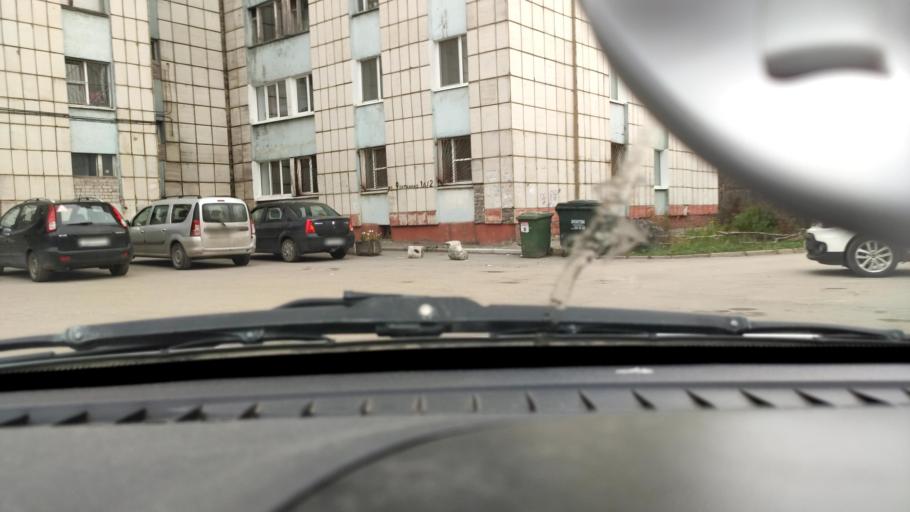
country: RU
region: Perm
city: Perm
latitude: 58.0021
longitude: 56.2780
